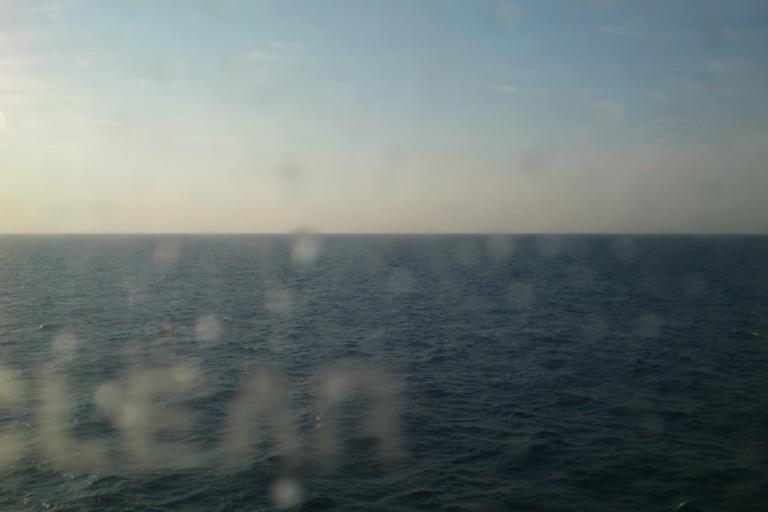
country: JP
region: Ishikawa
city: Nanao
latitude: 37.8261
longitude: 136.4550
